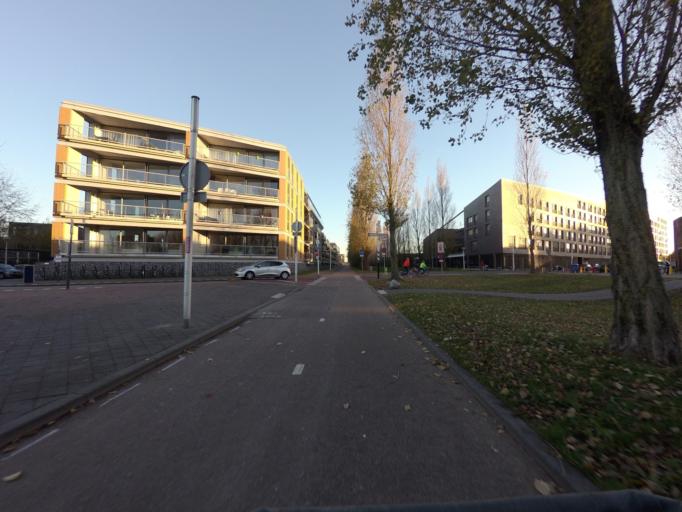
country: NL
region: Utrecht
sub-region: Stichtse Vecht
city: Maarssen
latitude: 52.1056
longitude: 5.0436
